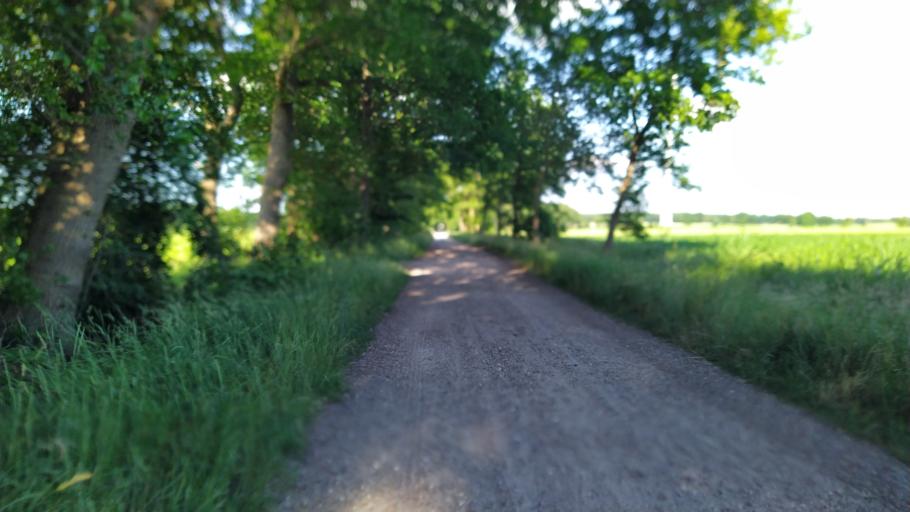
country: DE
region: Lower Saxony
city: Lintig
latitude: 53.5892
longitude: 8.9324
